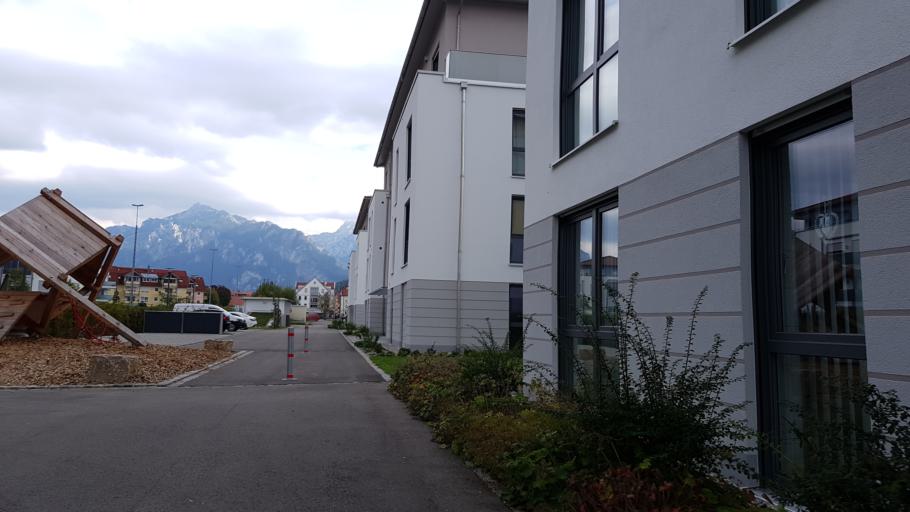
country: DE
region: Bavaria
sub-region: Swabia
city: Fuessen
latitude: 47.5714
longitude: 10.6935
